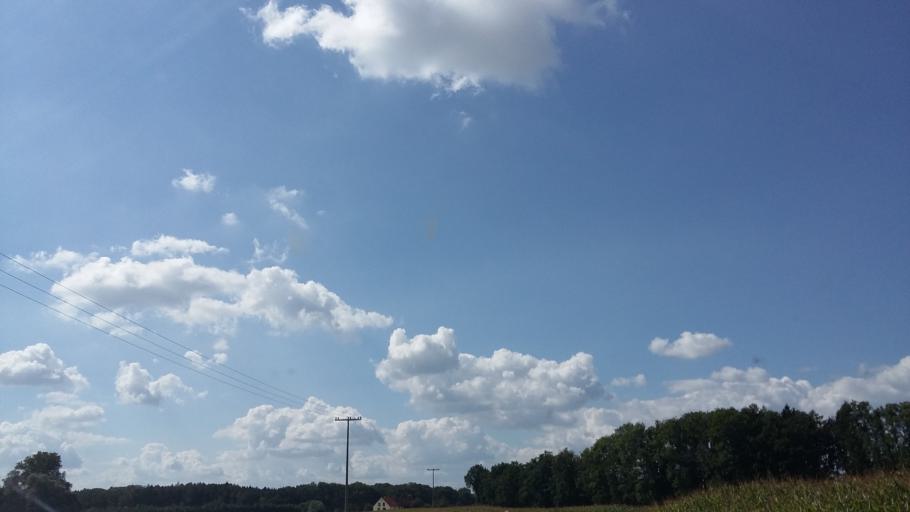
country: DE
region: Bavaria
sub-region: Swabia
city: Pfaffenhofen an der Roth
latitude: 48.3521
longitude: 10.1260
